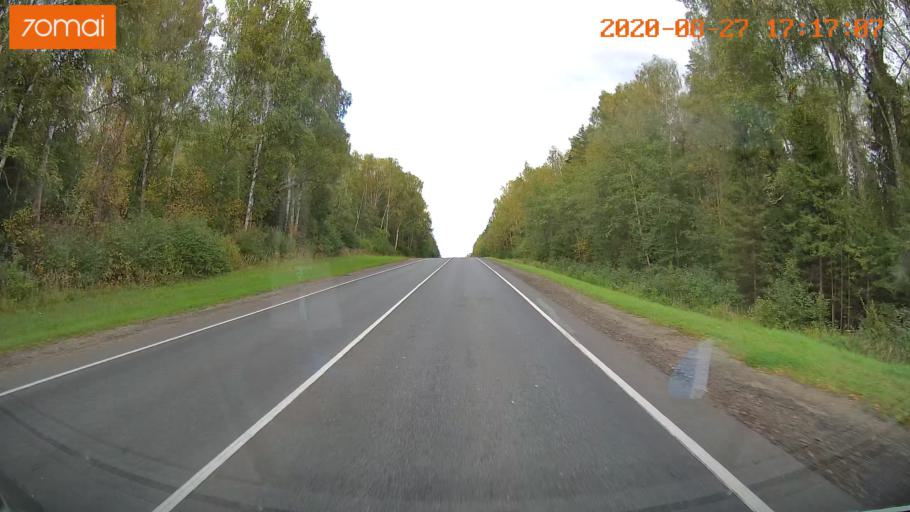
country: RU
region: Ivanovo
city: Lezhnevo
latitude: 56.7540
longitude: 40.7670
